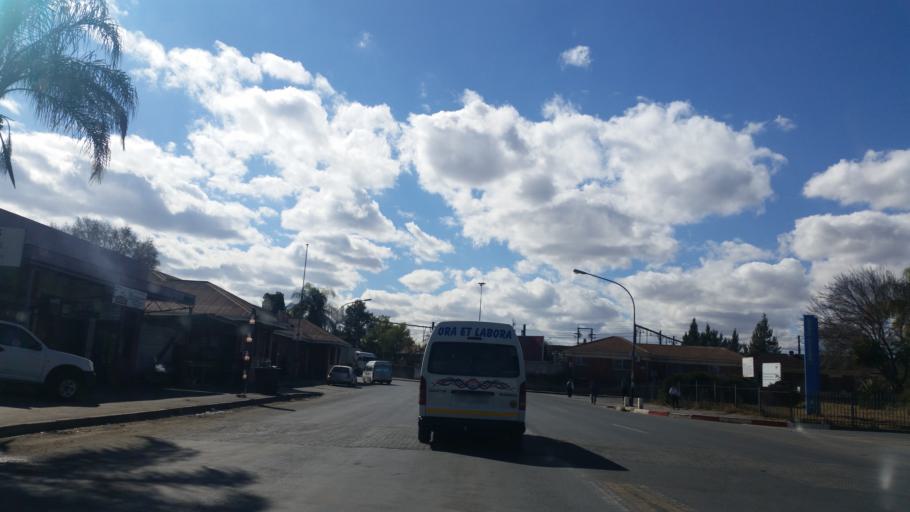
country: ZA
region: KwaZulu-Natal
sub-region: uThukela District Municipality
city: Ladysmith
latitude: -28.5580
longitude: 29.7848
